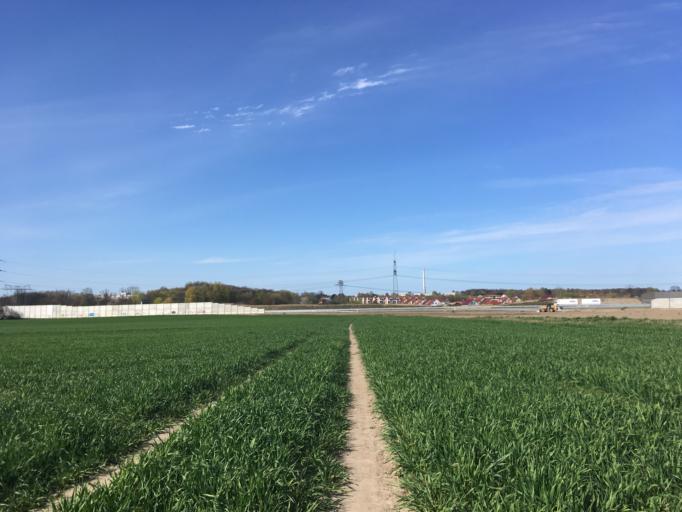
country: DE
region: Berlin
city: Buch
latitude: 52.6164
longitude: 13.5081
